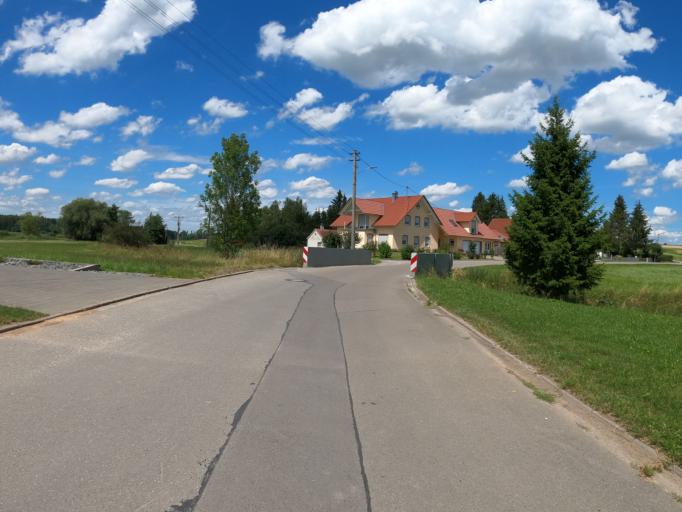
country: DE
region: Bavaria
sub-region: Swabia
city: Pfaffenhofen an der Roth
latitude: 48.4006
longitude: 10.1864
